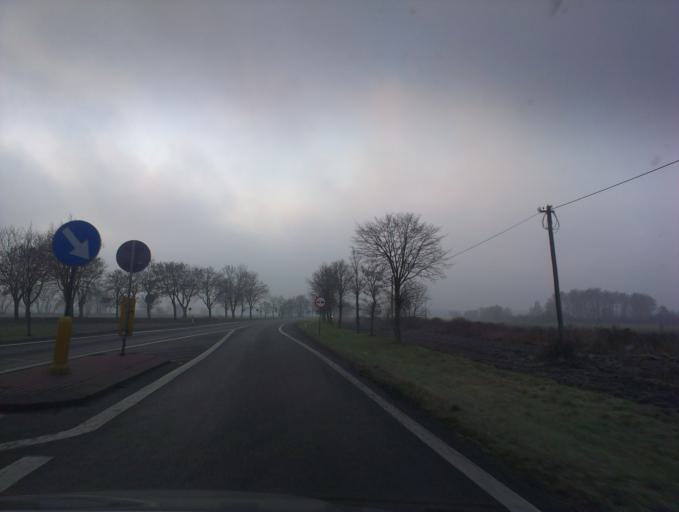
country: PL
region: Greater Poland Voivodeship
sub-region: Powiat chodzieski
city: Budzyn
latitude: 52.8713
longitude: 16.9759
